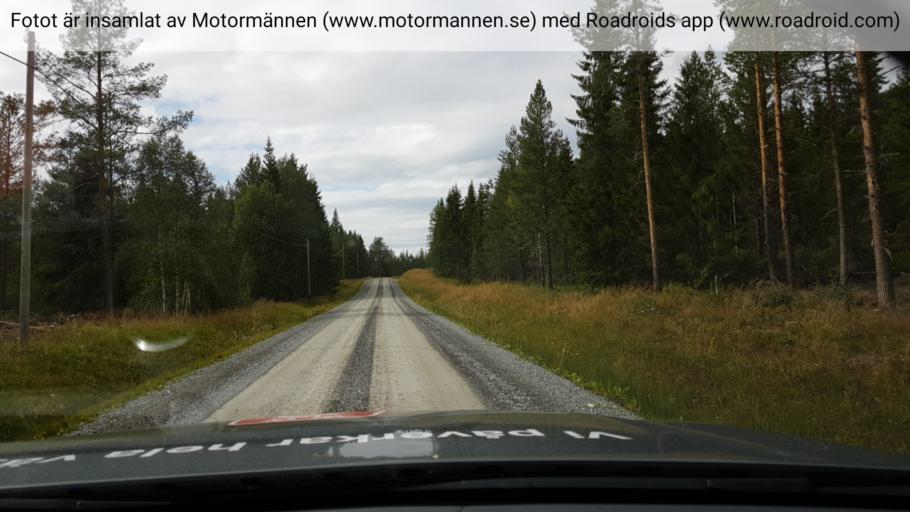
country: SE
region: Jaemtland
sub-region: Krokoms Kommun
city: Valla
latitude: 63.7087
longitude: 13.5553
